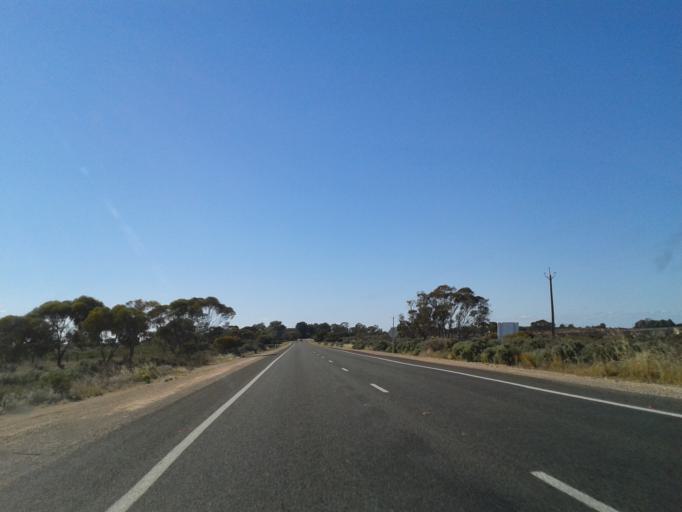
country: AU
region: South Australia
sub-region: Renmark Paringa
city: Renmark
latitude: -34.2271
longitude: 140.8206
